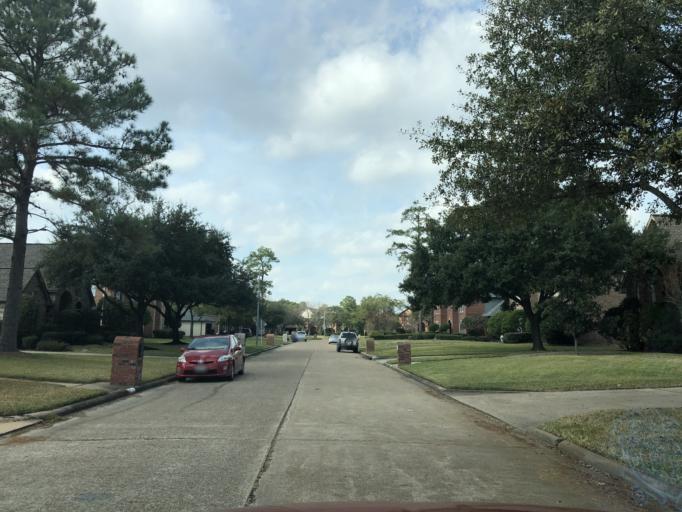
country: US
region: Texas
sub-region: Harris County
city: Tomball
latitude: 30.0310
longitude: -95.5383
